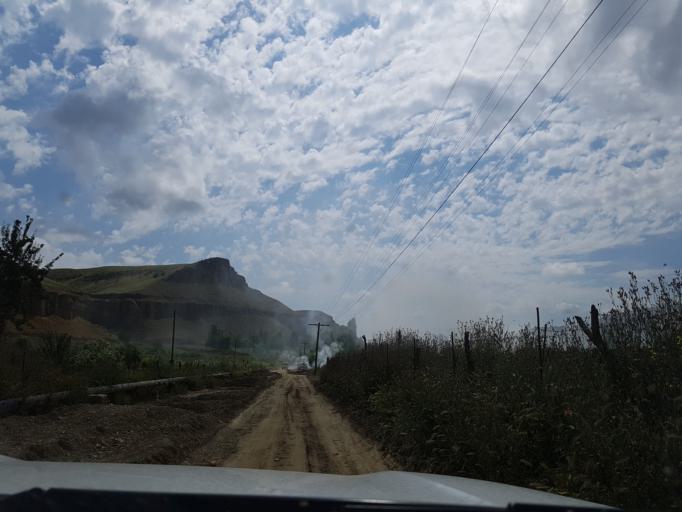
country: TM
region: Ahal
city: Baharly
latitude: 38.2262
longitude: 56.8775
